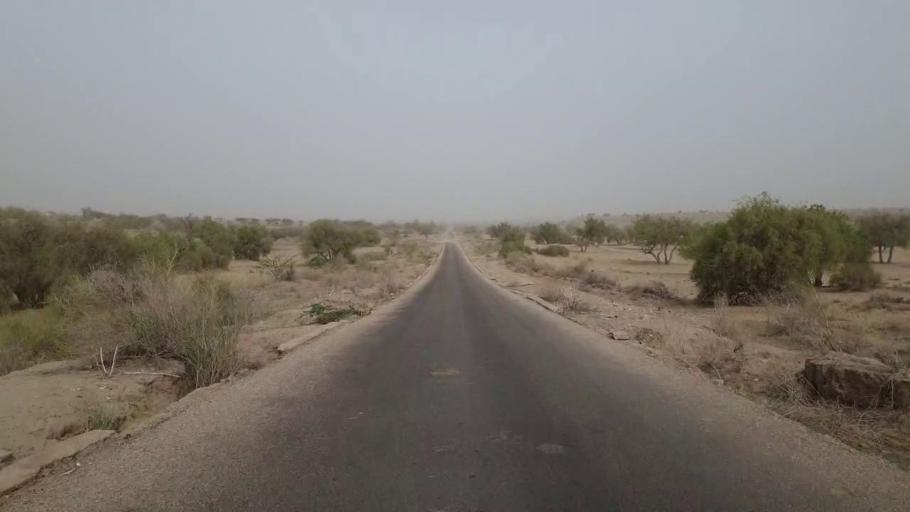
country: PK
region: Sindh
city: Islamkot
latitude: 24.5825
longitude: 70.2999
